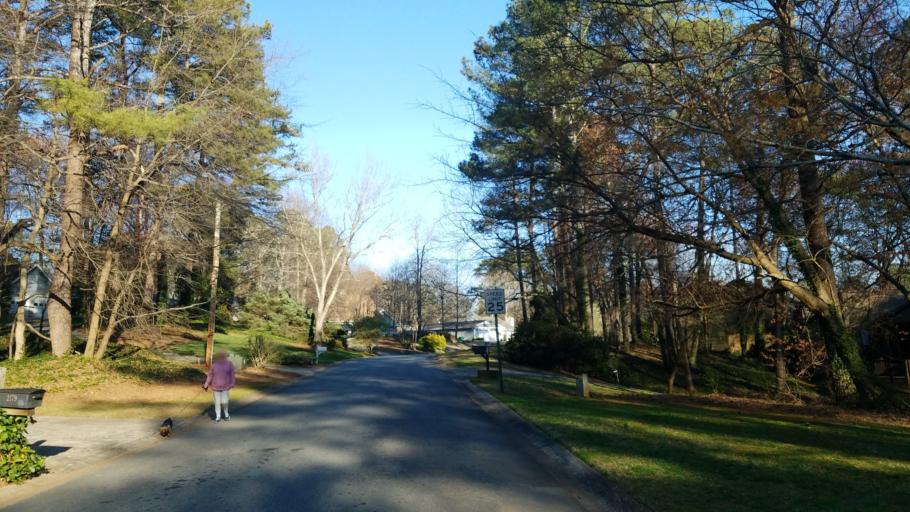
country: US
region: Georgia
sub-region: Cobb County
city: Marietta
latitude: 33.9968
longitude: -84.4902
